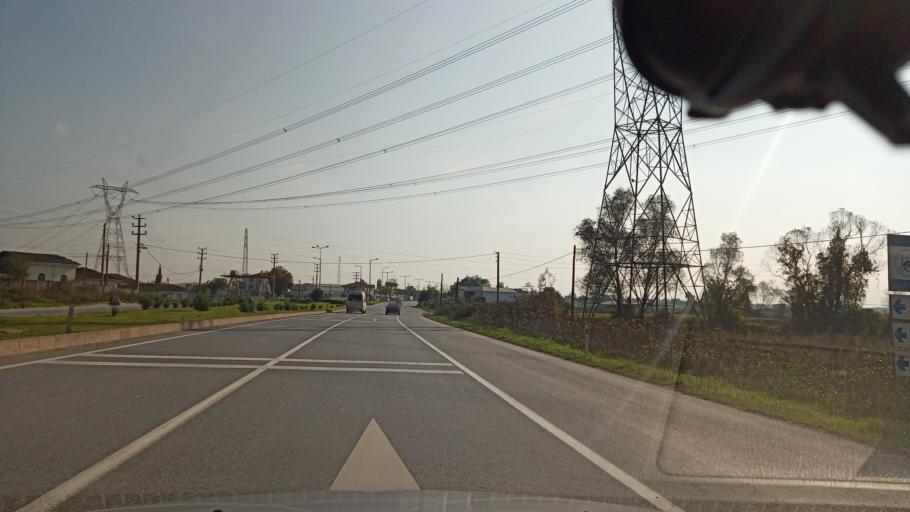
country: TR
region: Sakarya
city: Adapazari
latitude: 40.8223
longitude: 30.3955
